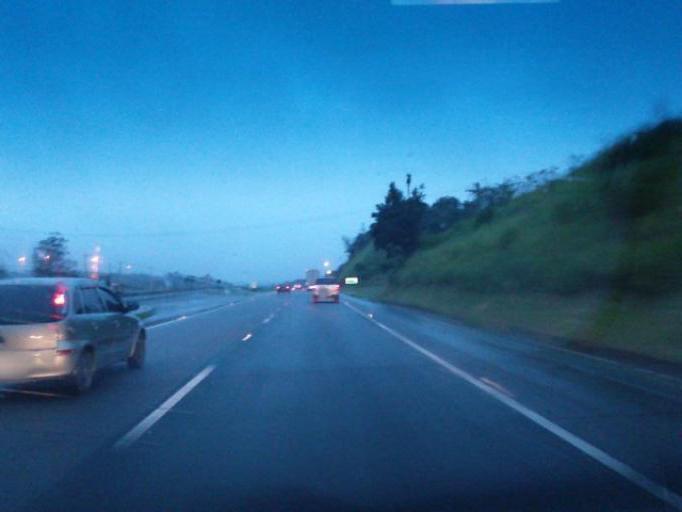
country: BR
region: Sao Paulo
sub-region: Juquitiba
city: Juquitiba
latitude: -23.9356
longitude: -47.0728
